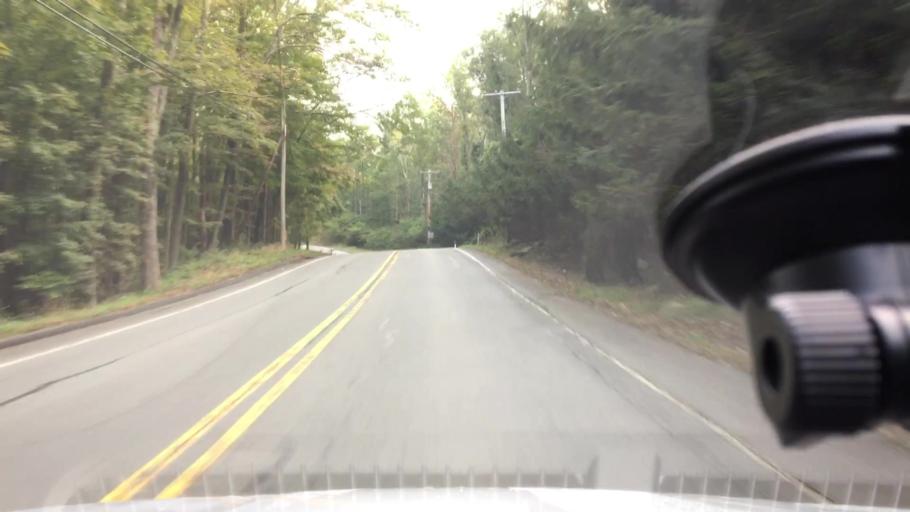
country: US
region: Pennsylvania
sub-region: Monroe County
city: Parkside
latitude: 41.1250
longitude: -75.2793
